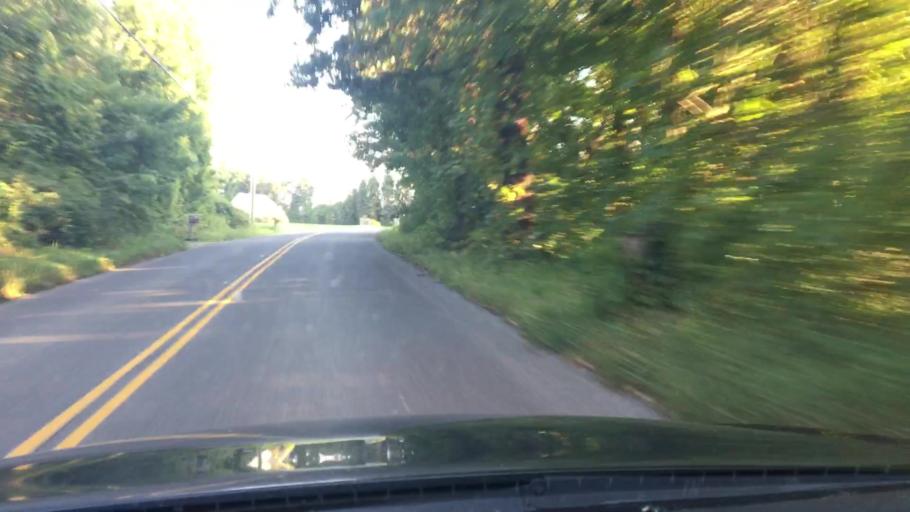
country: US
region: Connecticut
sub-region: Litchfield County
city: New Milford
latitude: 41.6139
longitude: -73.3726
